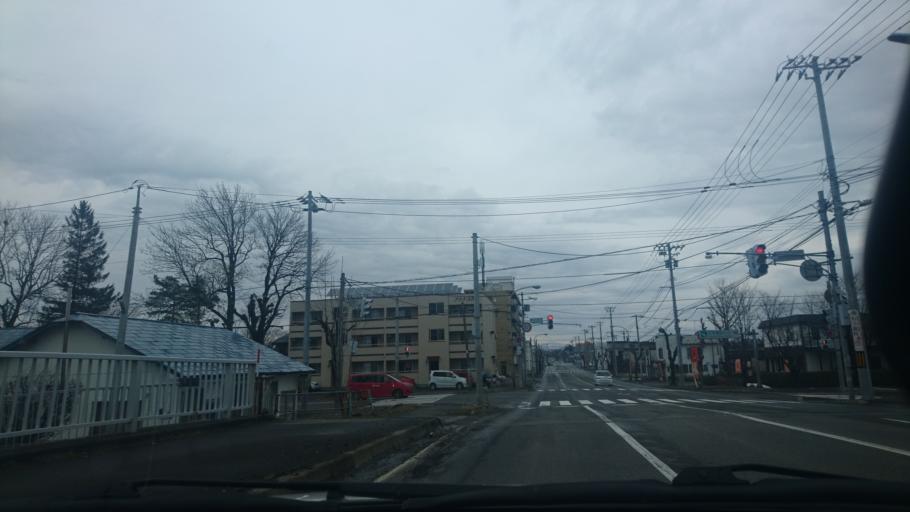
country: JP
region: Hokkaido
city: Obihiro
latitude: 42.9288
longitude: 143.1964
